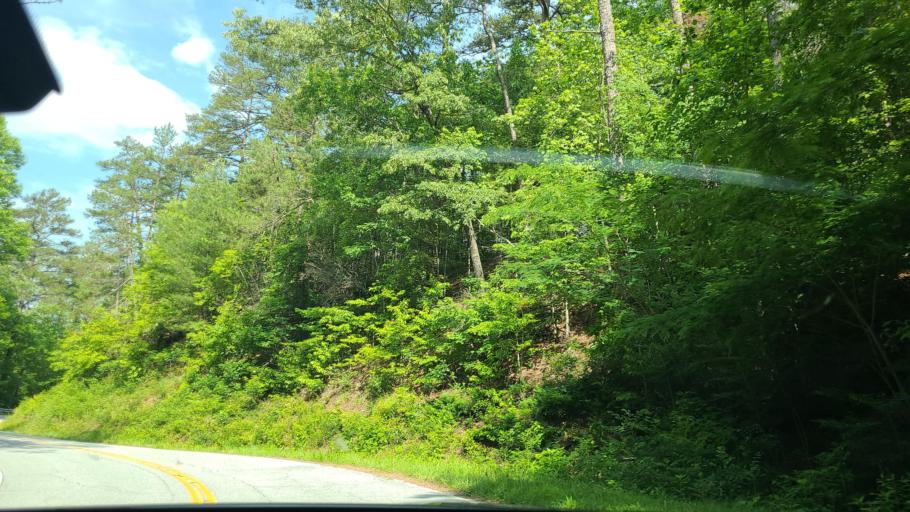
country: US
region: South Carolina
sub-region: Oconee County
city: Walhalla
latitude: 34.8997
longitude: -83.1801
